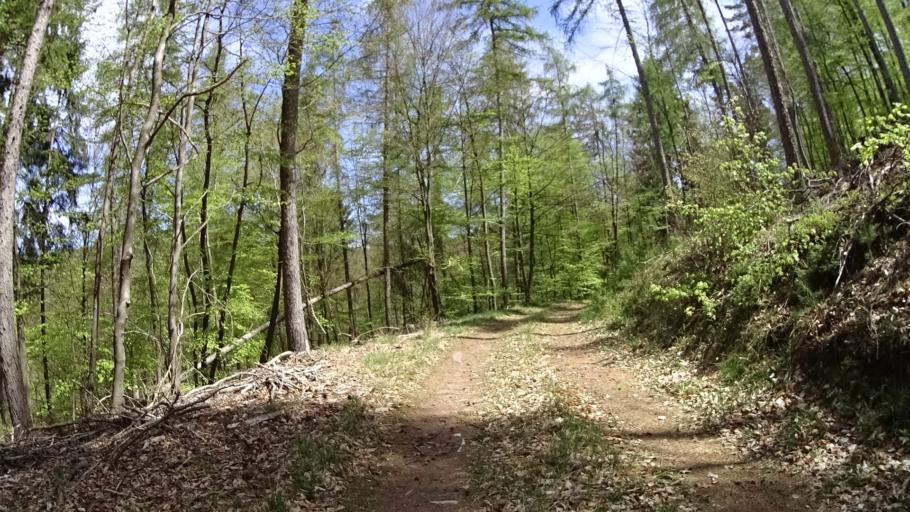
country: DE
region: Rheinland-Pfalz
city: Ramberg
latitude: 49.3112
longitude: 8.0051
